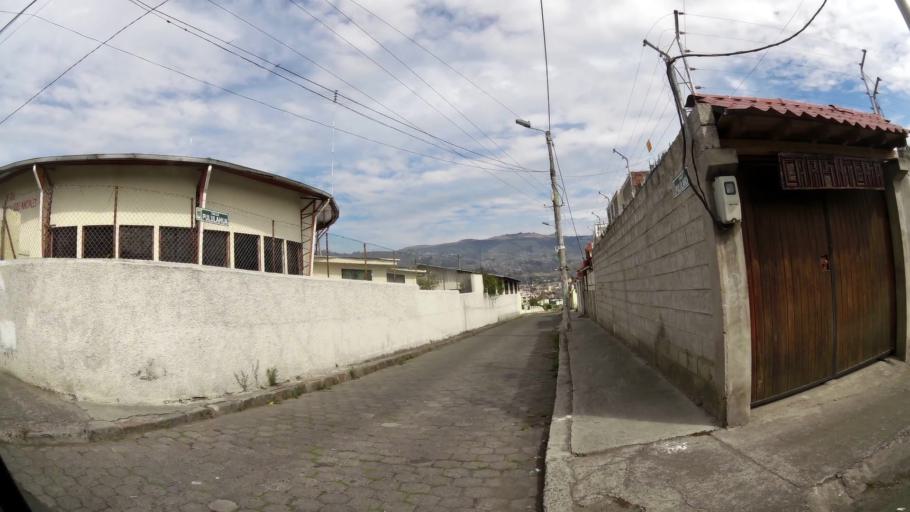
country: EC
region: Tungurahua
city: Ambato
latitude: -1.2451
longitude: -78.6248
